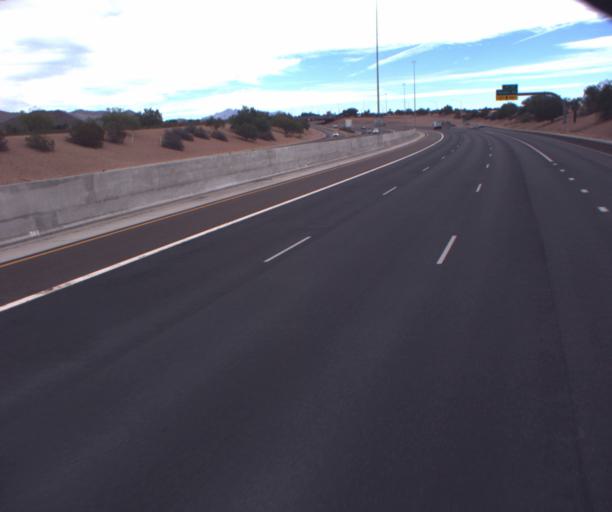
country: US
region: Arizona
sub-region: Maricopa County
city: Mesa
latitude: 33.4772
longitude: -111.7091
